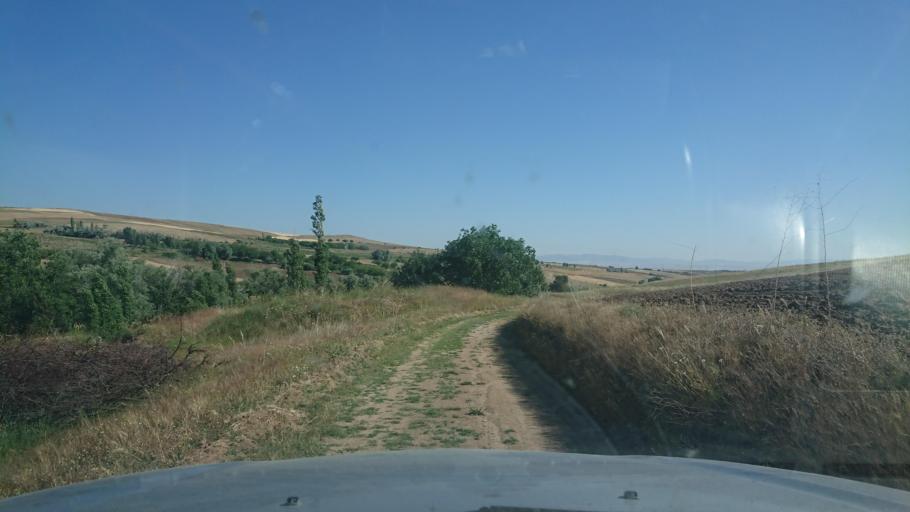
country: TR
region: Aksaray
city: Agacoren
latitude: 38.8413
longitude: 33.9257
